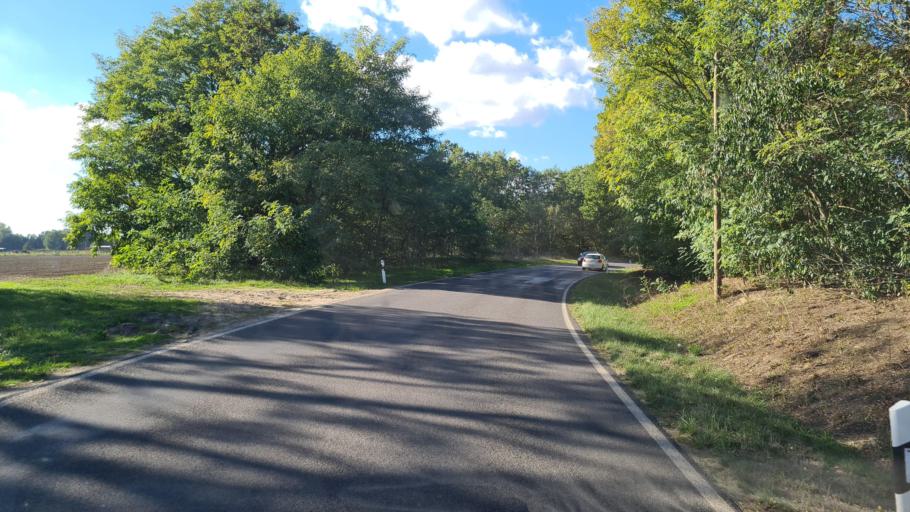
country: DE
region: Brandenburg
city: Kolkwitz
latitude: 51.7635
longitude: 14.2691
